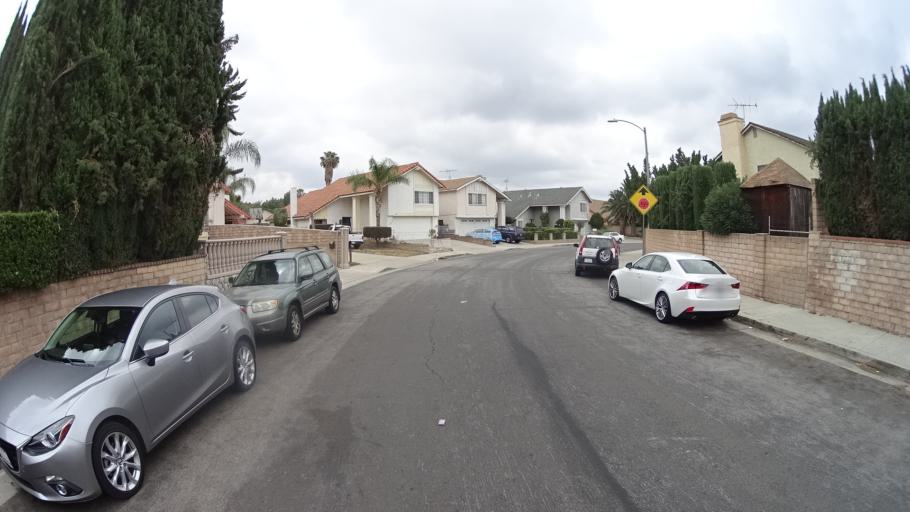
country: US
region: California
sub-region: Los Angeles County
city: San Fernando
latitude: 34.2782
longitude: -118.4591
